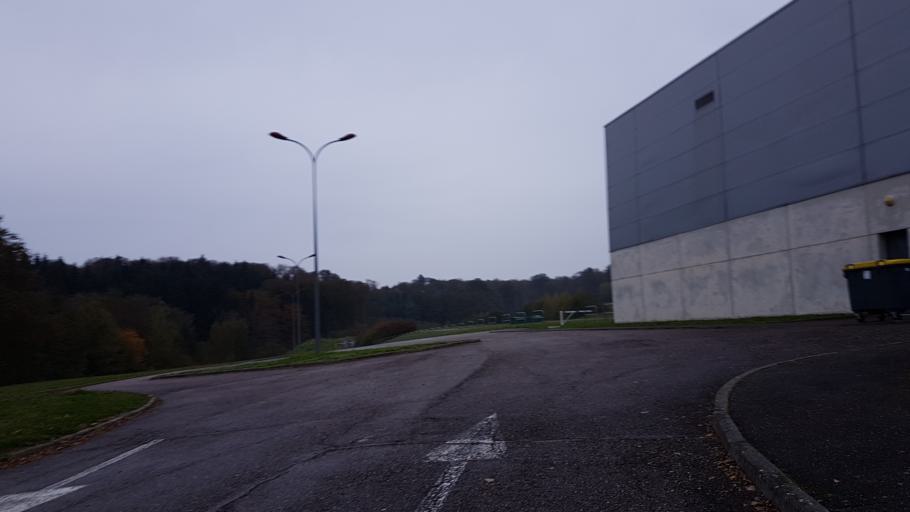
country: FR
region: Franche-Comte
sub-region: Departement de la Haute-Saone
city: Luxeuil-les-Bains
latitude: 47.8259
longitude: 6.3736
